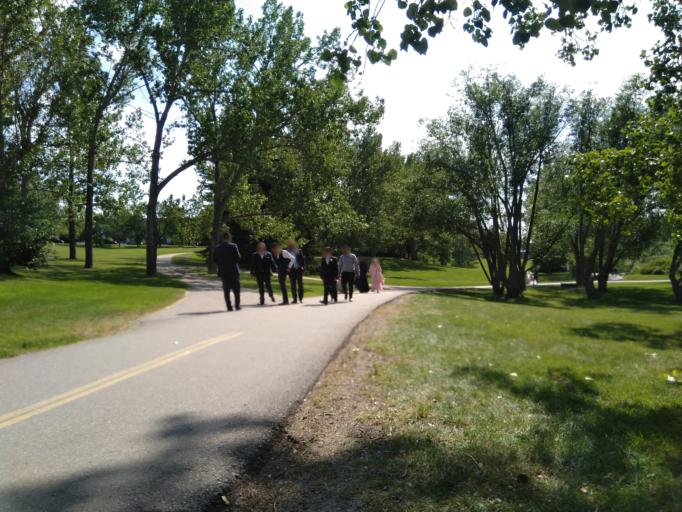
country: CA
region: Alberta
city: Calgary
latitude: 51.0748
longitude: -114.0859
